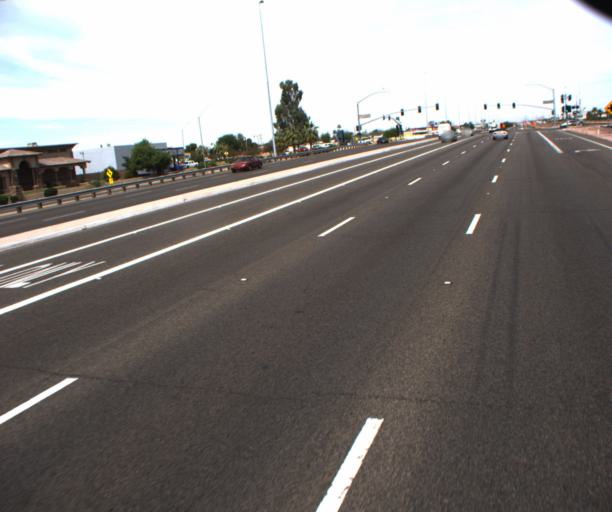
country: US
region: Arizona
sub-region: Maricopa County
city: Surprise
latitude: 33.6228
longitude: -112.3296
